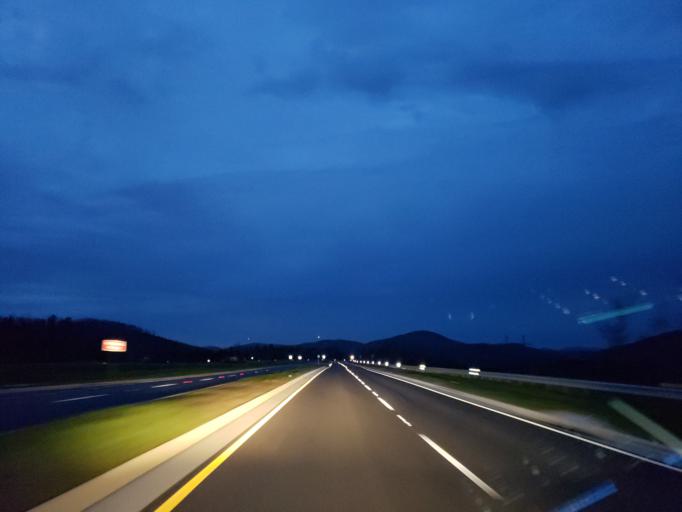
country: US
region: Georgia
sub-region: Bartow County
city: Emerson
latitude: 34.1348
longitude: -84.7409
